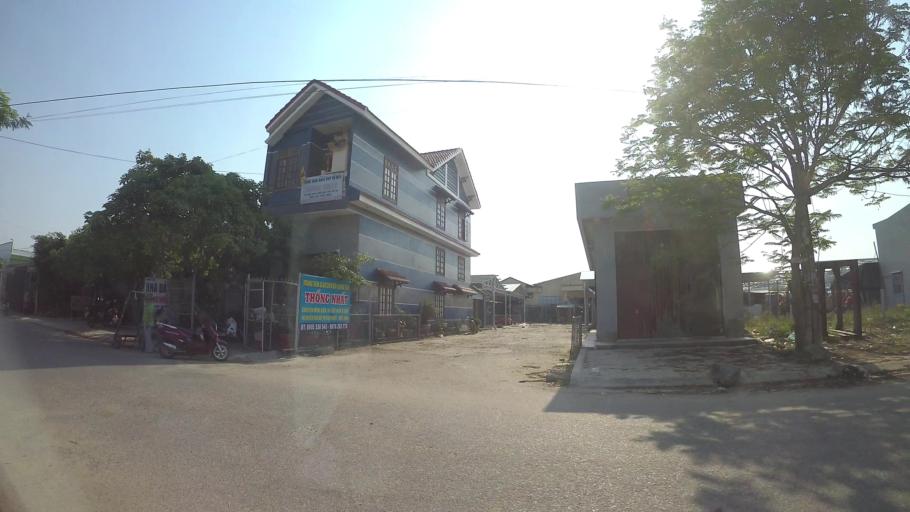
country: VN
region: Da Nang
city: Ngu Hanh Son
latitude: 15.9536
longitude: 108.2594
